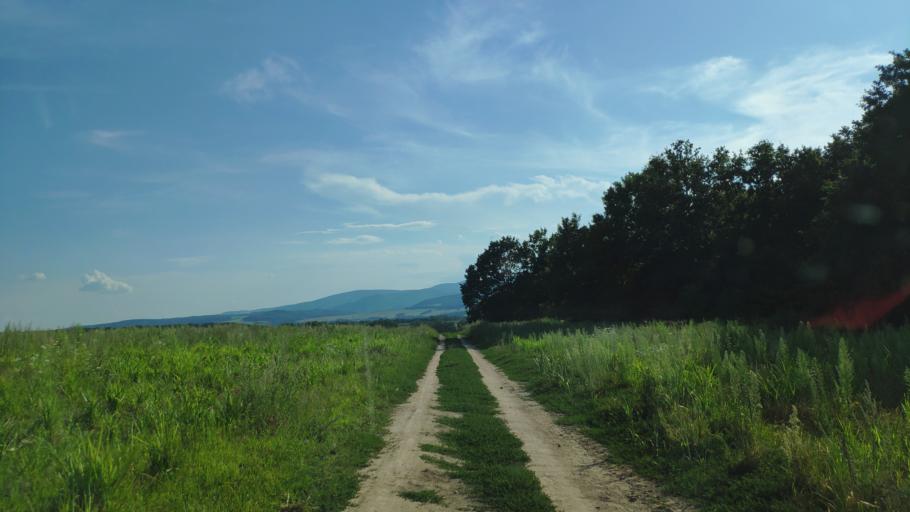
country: SK
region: Presovsky
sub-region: Okres Presov
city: Presov
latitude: 48.9143
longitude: 21.2818
